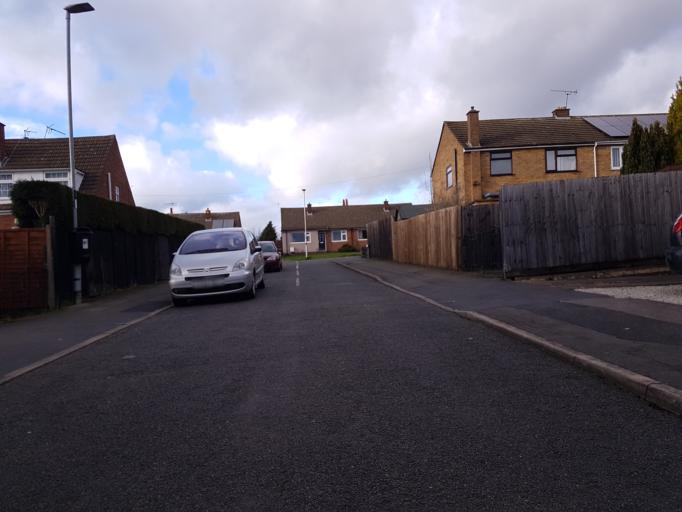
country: GB
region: England
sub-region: Leicestershire
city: Earl Shilton
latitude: 52.5687
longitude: -1.3234
